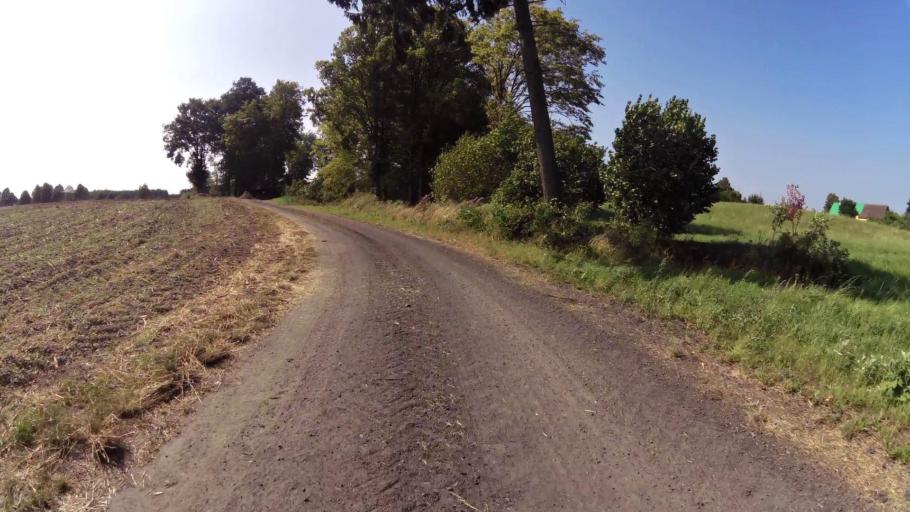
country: PL
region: West Pomeranian Voivodeship
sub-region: Powiat walecki
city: Walcz
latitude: 53.3301
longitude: 16.3025
